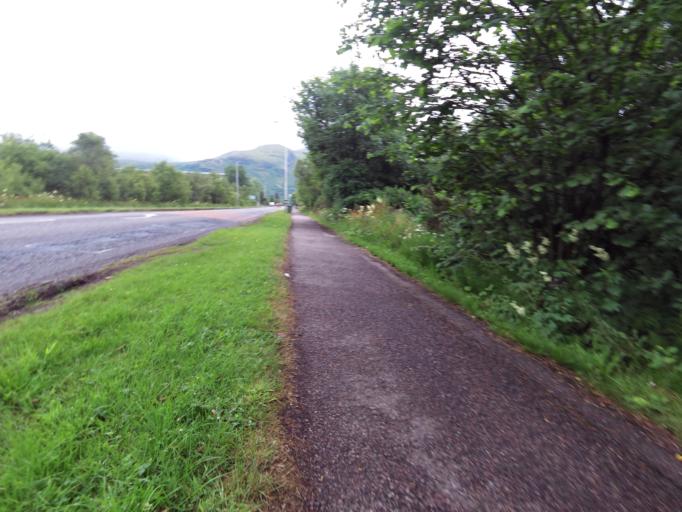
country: GB
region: Scotland
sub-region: Highland
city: Fort William
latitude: 56.8386
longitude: -5.0822
